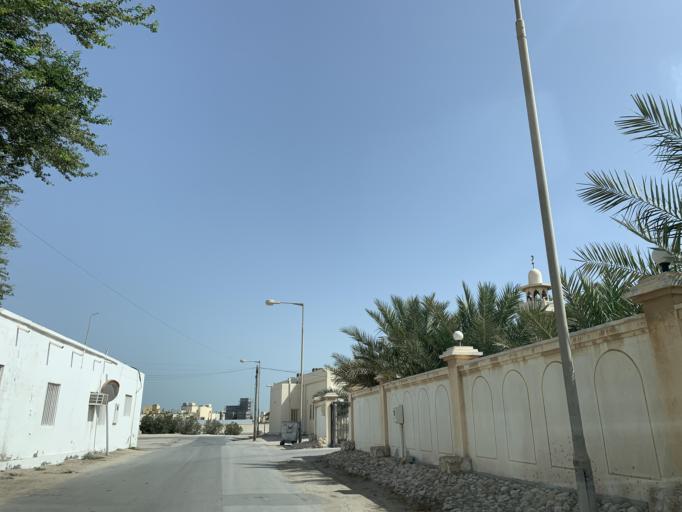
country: BH
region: Northern
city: Sitrah
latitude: 26.1464
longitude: 50.6020
